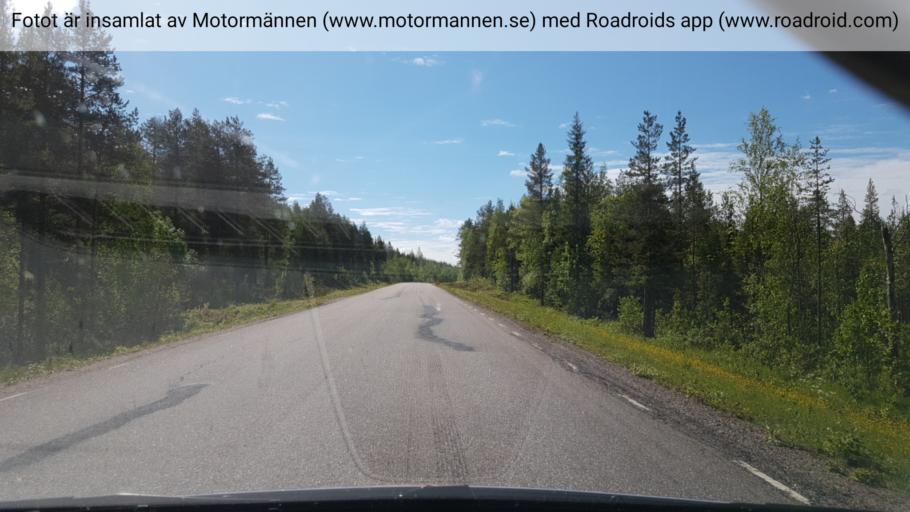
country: FI
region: Lapland
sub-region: Torniolaakso
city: Pello
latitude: 66.7280
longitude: 23.8653
